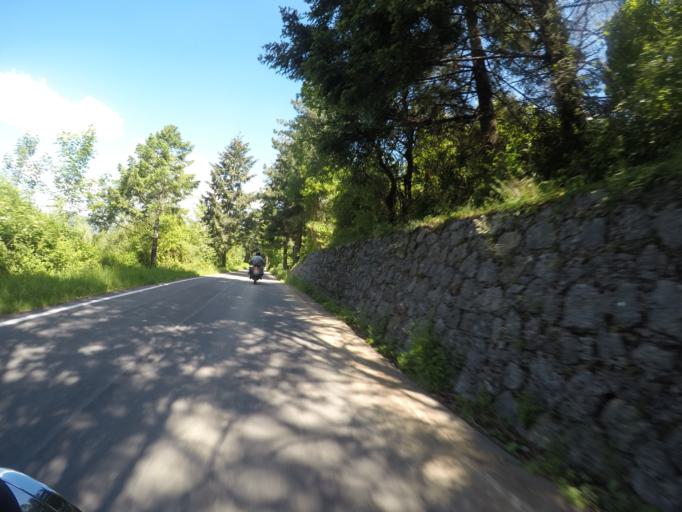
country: IT
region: Tuscany
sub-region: Provincia di Lucca
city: Careggine
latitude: 44.1084
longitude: 10.3333
